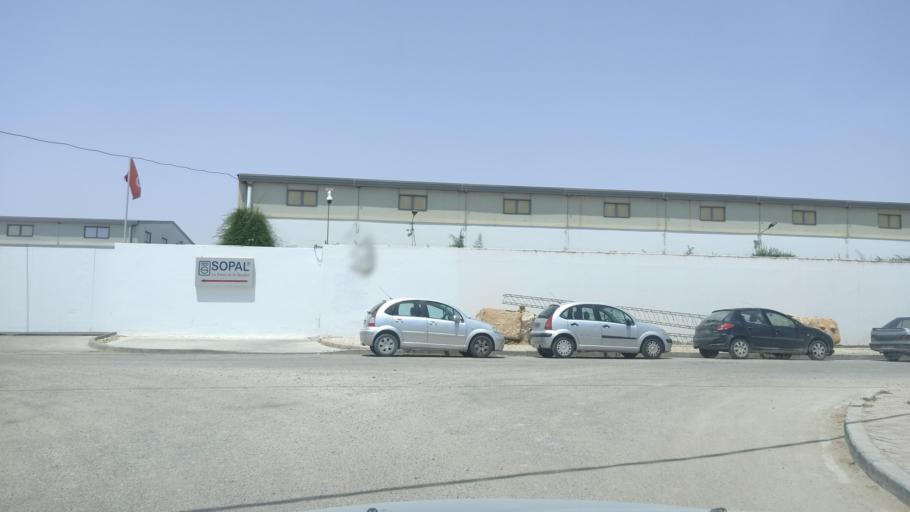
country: TN
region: Safaqis
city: Sfax
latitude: 34.6648
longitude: 10.6966
